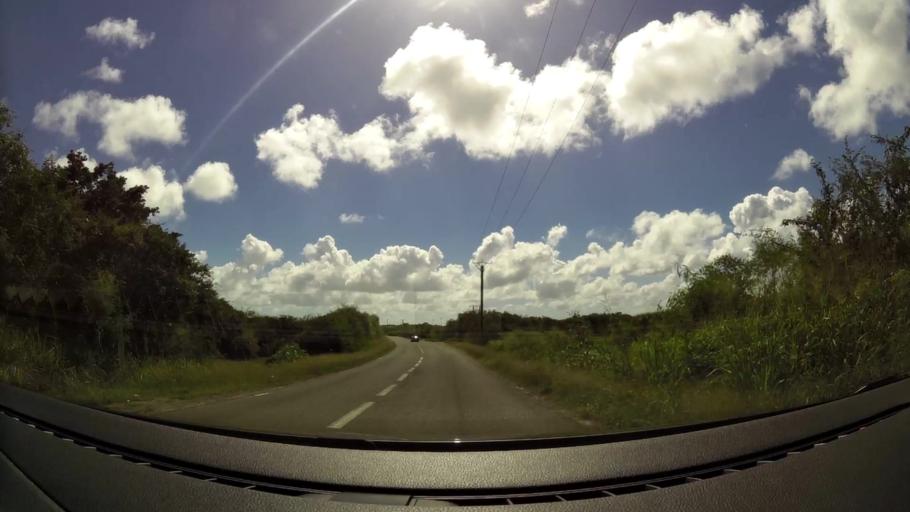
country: GP
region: Guadeloupe
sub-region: Guadeloupe
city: Anse-Bertrand
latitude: 16.4299
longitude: -61.4769
